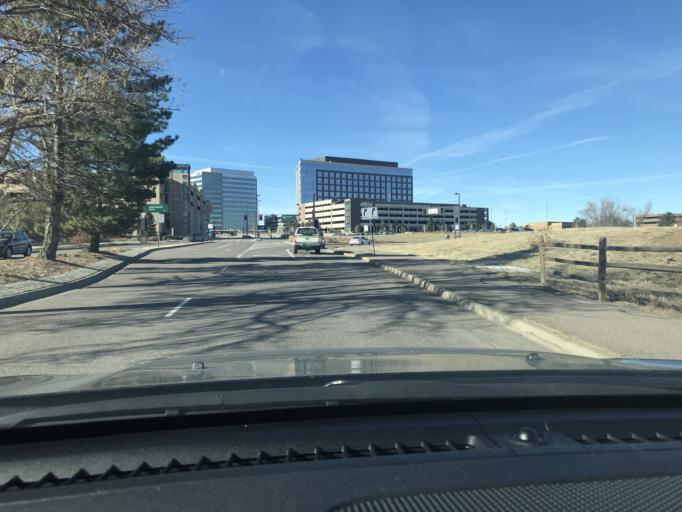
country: US
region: Colorado
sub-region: Arapahoe County
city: Centennial
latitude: 39.6024
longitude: -104.8841
